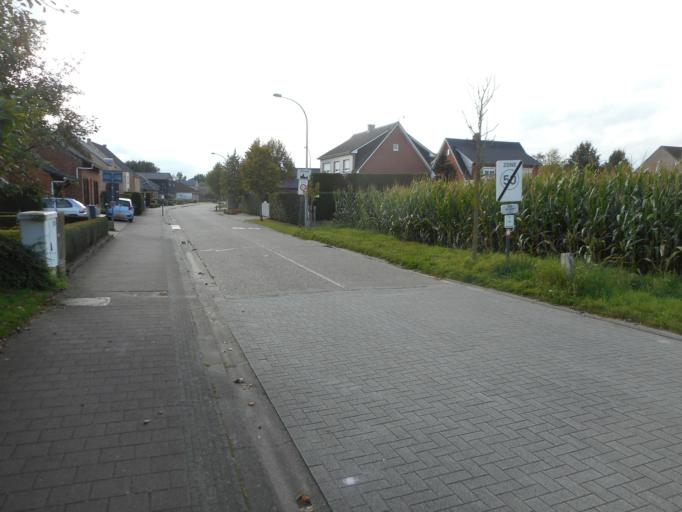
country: BE
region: Flanders
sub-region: Provincie Antwerpen
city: Oostmalle
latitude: 51.2940
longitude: 4.7868
